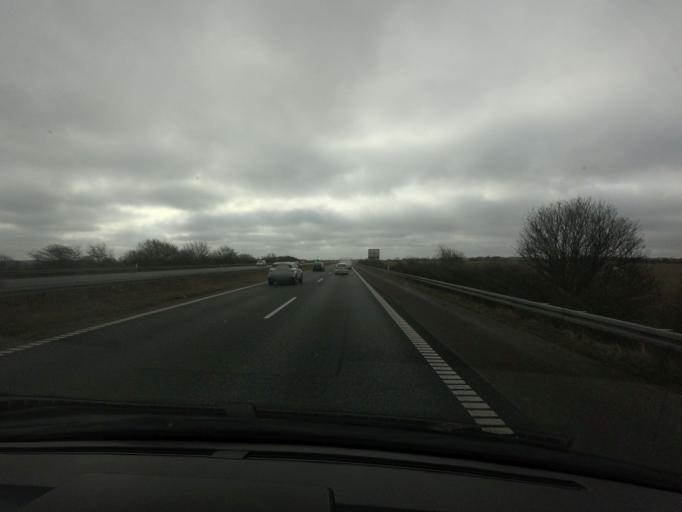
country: DK
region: South Denmark
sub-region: Kolding Kommune
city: Christiansfeld
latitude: 55.3832
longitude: 9.4498
